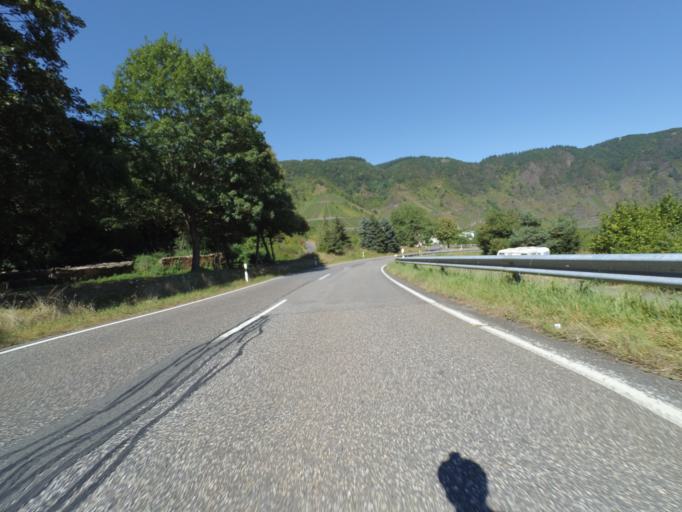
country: DE
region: Rheinland-Pfalz
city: Bremm
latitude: 50.0966
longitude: 7.1164
